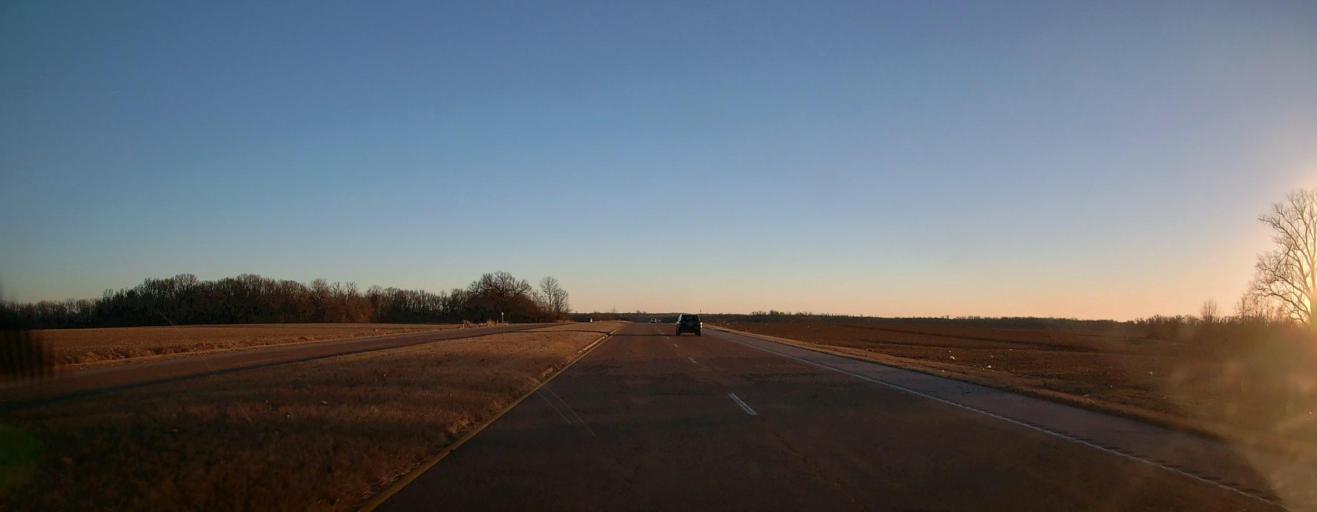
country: US
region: Tennessee
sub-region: Shelby County
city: Millington
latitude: 35.2988
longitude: -89.8822
